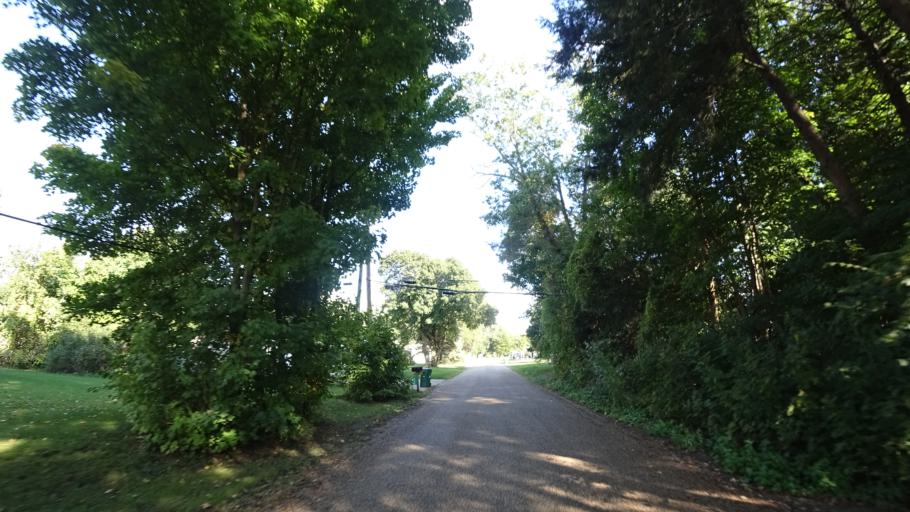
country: US
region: Michigan
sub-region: Saint Joseph County
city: Three Rivers
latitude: 41.9599
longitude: -85.6343
